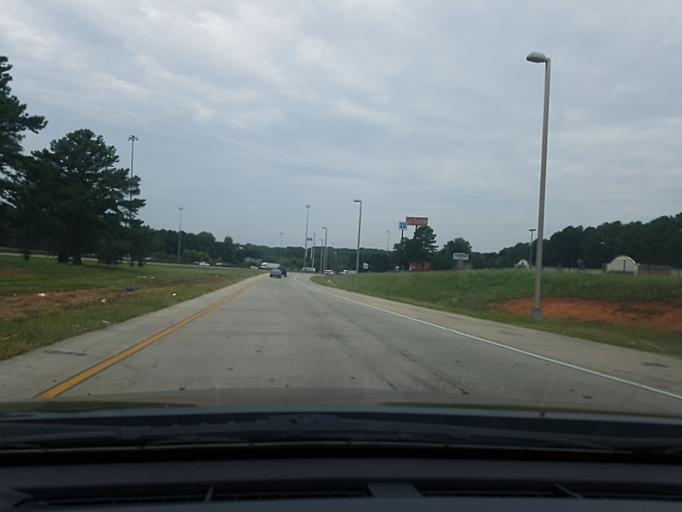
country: US
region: Georgia
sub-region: Clayton County
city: Morrow
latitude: 33.5783
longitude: -84.3434
